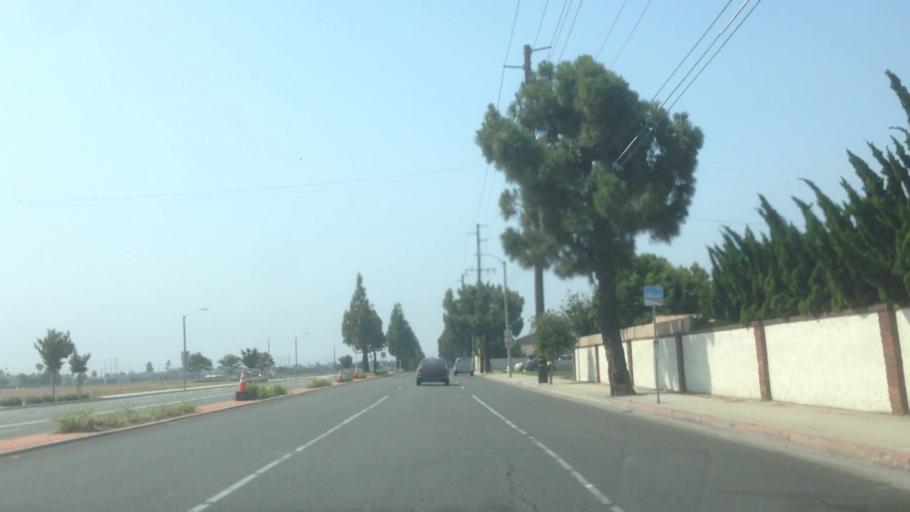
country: US
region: California
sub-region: Orange County
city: Fountain Valley
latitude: 33.7089
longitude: -117.9371
